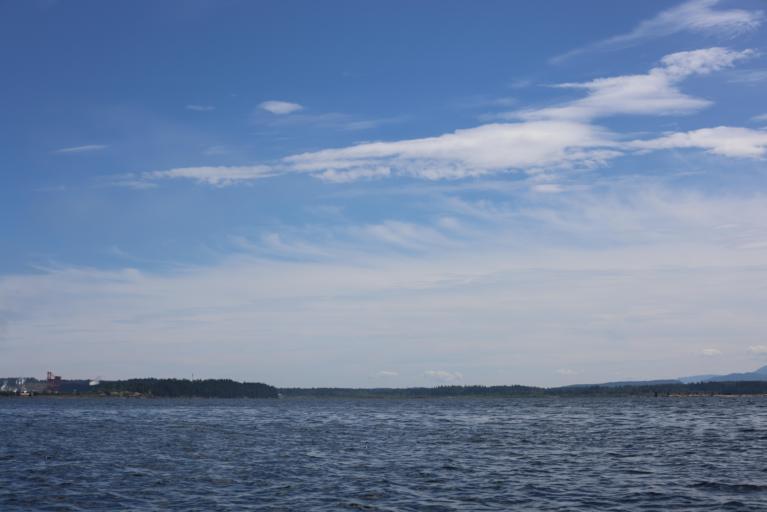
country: CA
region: British Columbia
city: Nanaimo
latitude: 49.1652
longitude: -123.9192
